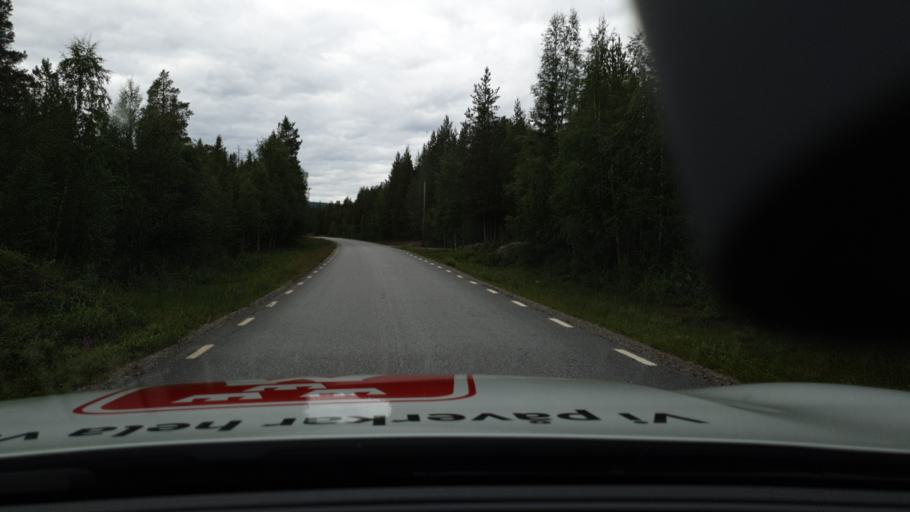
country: SE
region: Norrbotten
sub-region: Arjeplogs Kommun
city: Arjeplog
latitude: 66.8820
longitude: 18.2487
